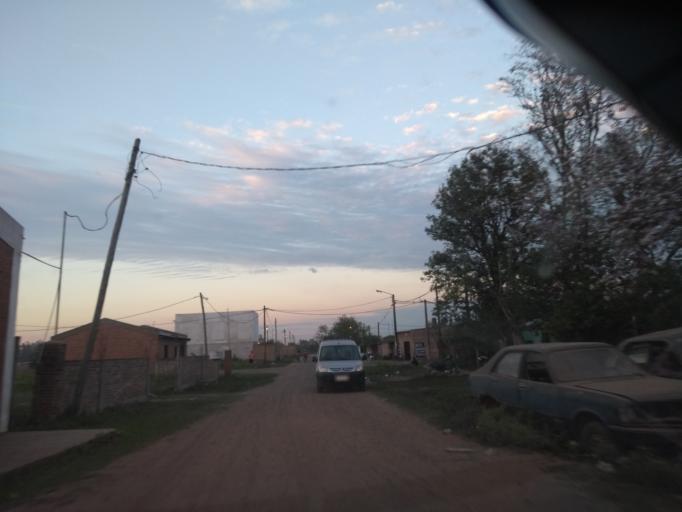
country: AR
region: Chaco
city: Fontana
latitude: -27.4041
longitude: -59.0450
